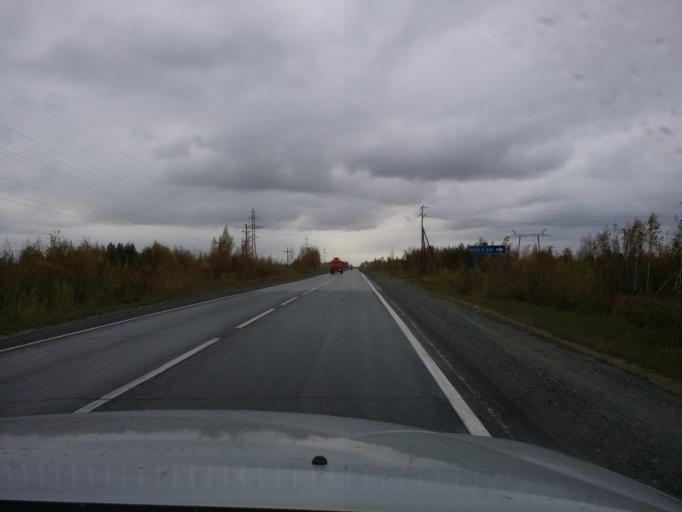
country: RU
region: Khanty-Mansiyskiy Avtonomnyy Okrug
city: Megion
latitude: 61.1029
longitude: 75.9502
